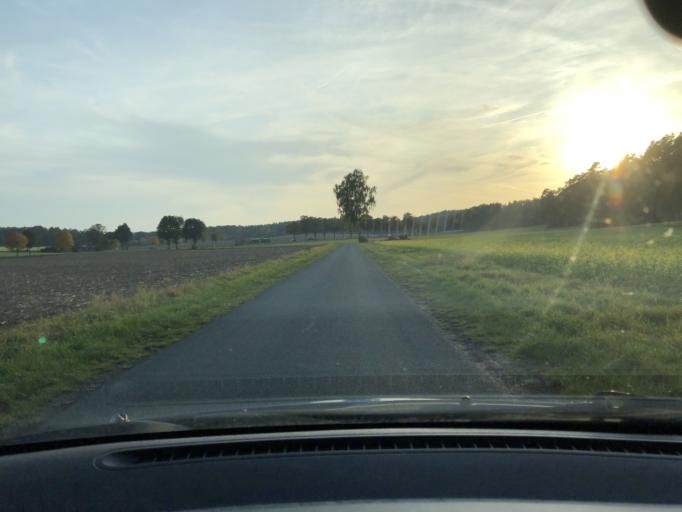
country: DE
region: Lower Saxony
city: Gohrde
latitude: 53.1322
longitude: 10.9477
